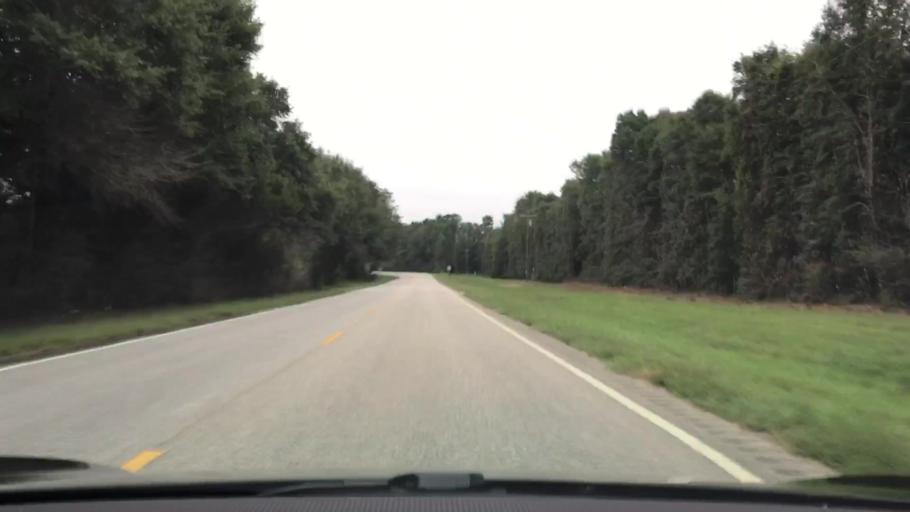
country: US
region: Alabama
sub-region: Coffee County
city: Elba
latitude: 31.3806
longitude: -86.0883
